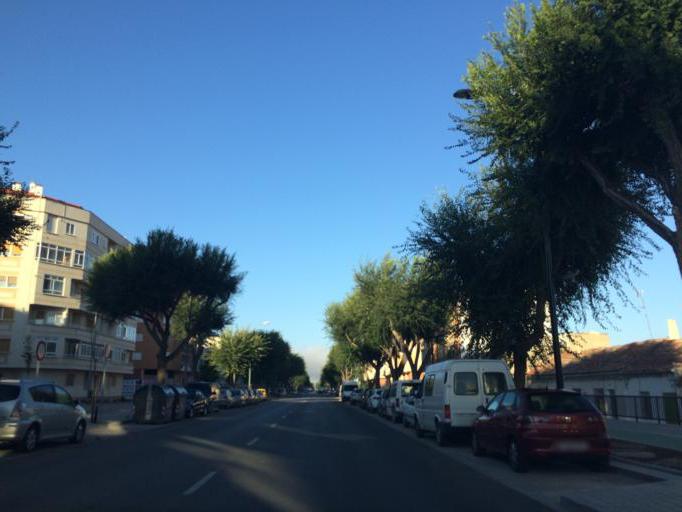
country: ES
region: Castille-La Mancha
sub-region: Provincia de Albacete
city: Albacete
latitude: 39.0031
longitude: -1.8675
